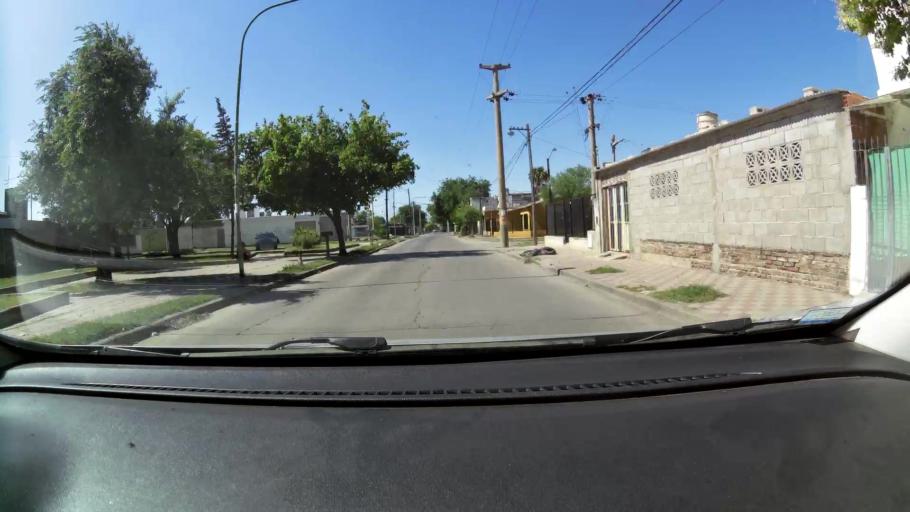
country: AR
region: Cordoba
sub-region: Departamento de Capital
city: Cordoba
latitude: -31.3723
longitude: -64.1558
